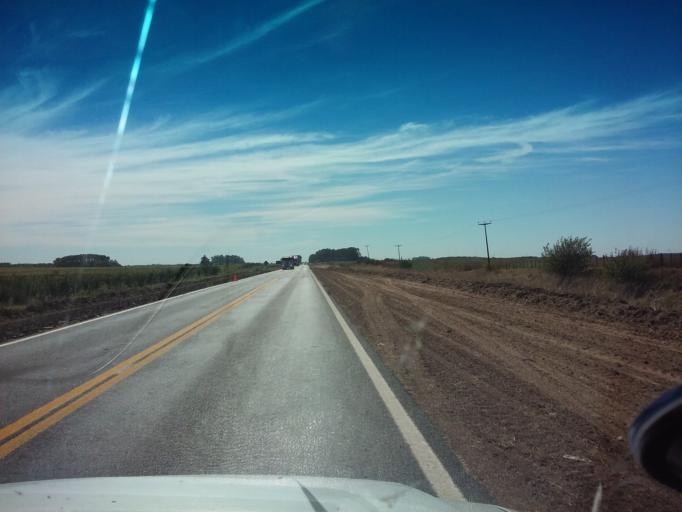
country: AR
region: Buenos Aires
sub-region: Partido de Nueve de Julio
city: Nueve de Julio
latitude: -35.3532
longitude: -60.6943
